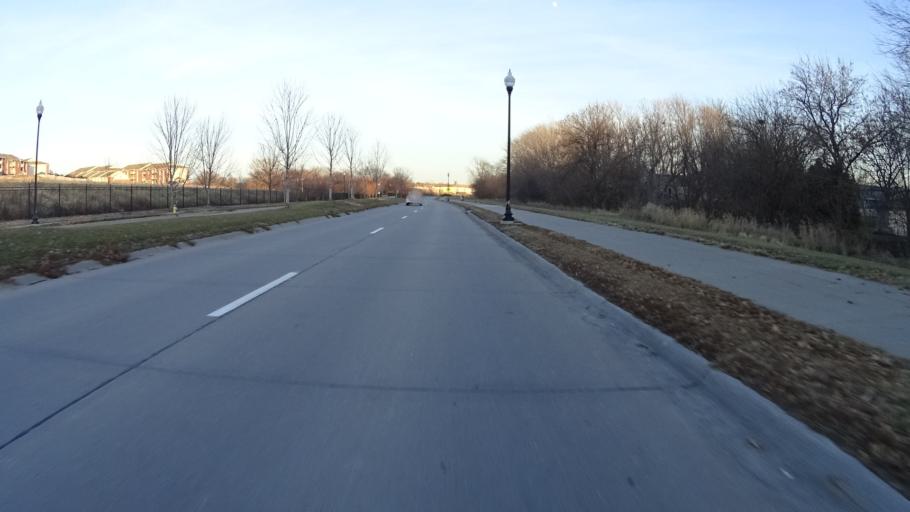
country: US
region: Nebraska
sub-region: Sarpy County
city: Papillion
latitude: 41.1329
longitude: -96.0392
